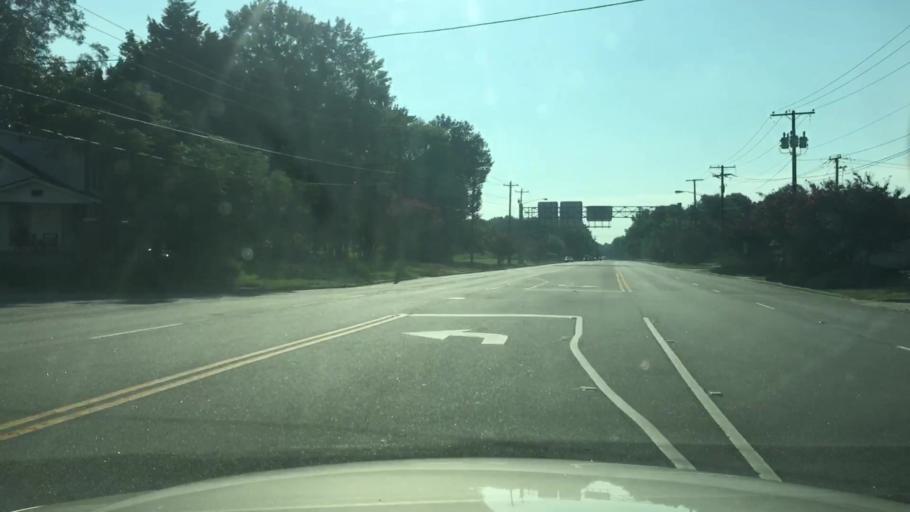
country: US
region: North Carolina
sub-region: Cumberland County
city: Fayetteville
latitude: 35.0523
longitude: -78.8627
